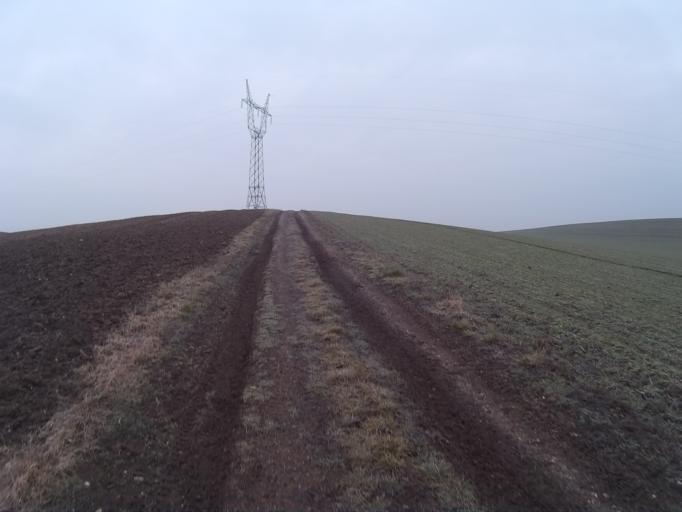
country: HU
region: Komarom-Esztergom
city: Tarjan
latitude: 47.6289
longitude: 18.4959
